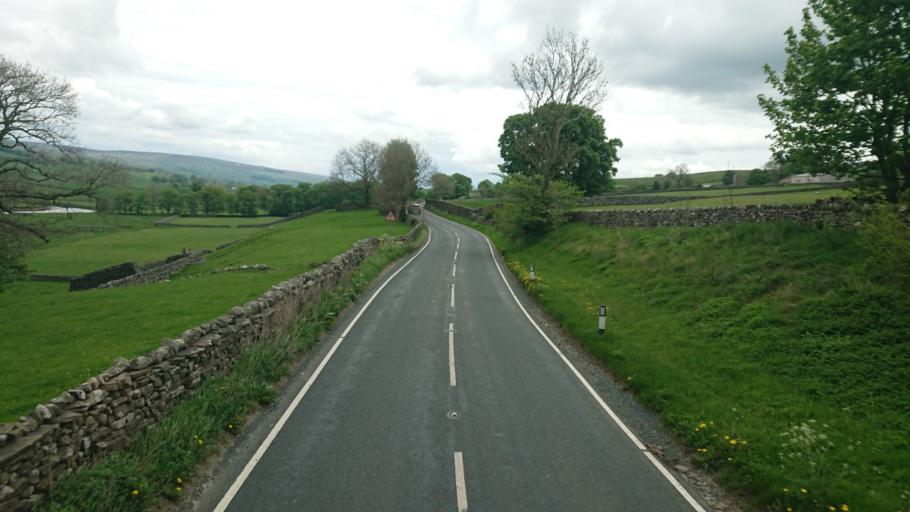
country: GB
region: England
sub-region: Cumbria
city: Kirkby Stephen
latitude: 54.3026
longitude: -2.1706
